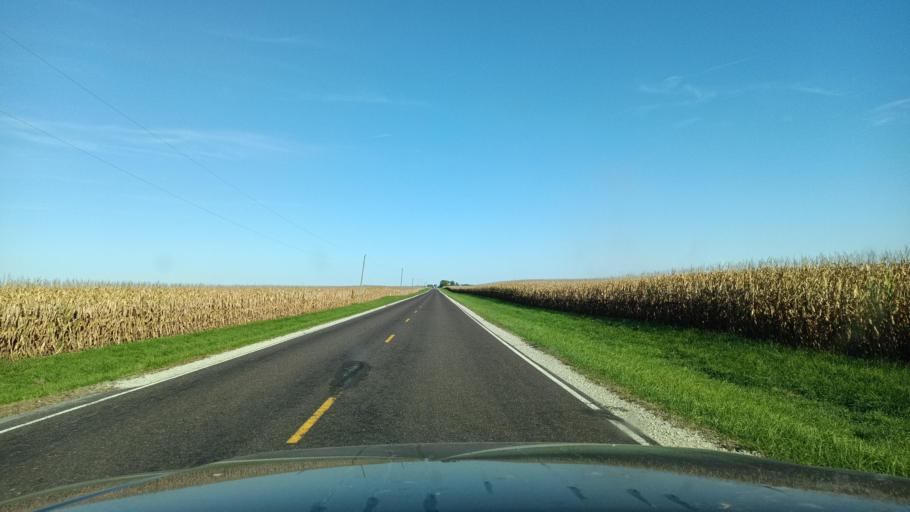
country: US
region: Illinois
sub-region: McLean County
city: Heyworth
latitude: 40.2315
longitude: -89.0479
